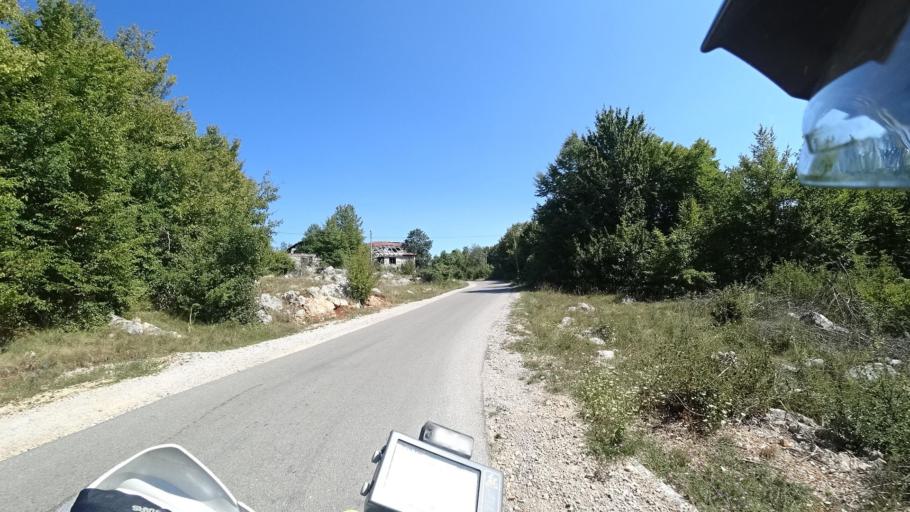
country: HR
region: Licko-Senjska
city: Popovaca
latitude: 44.7294
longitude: 15.2877
